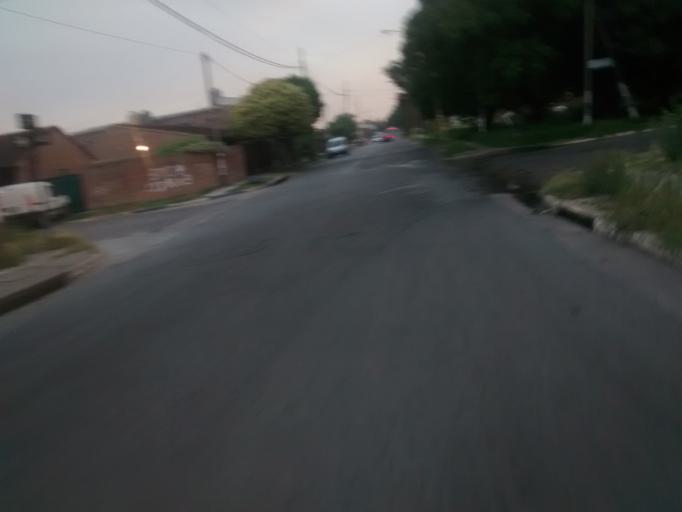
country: AR
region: Buenos Aires
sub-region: Partido de La Plata
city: La Plata
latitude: -34.9414
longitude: -57.9208
